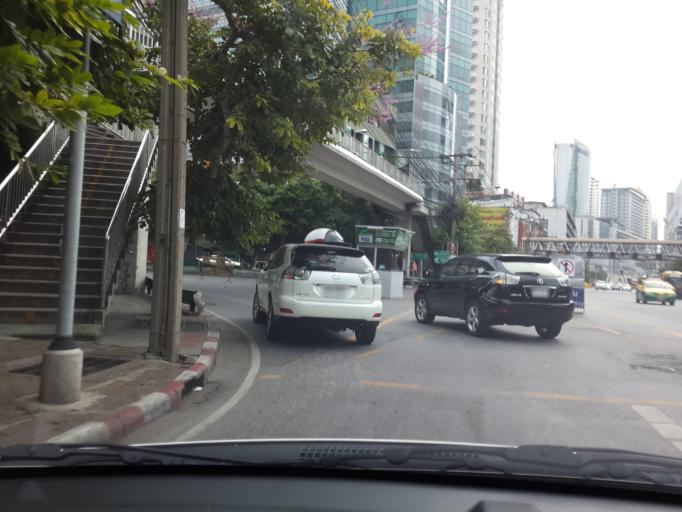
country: TH
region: Bangkok
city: Ratchathewi
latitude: 13.7494
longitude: 100.5451
